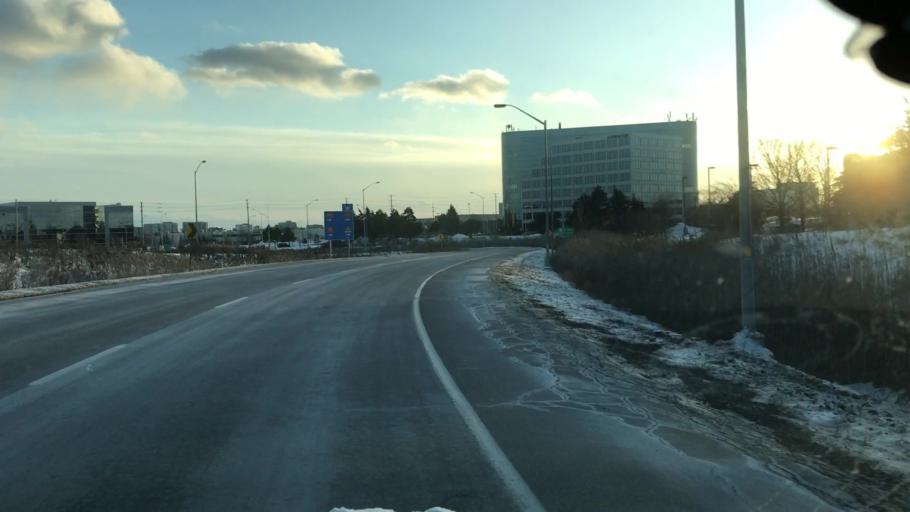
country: CA
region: Ontario
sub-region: York
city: Richmond Hill
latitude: 43.8669
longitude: -79.3773
